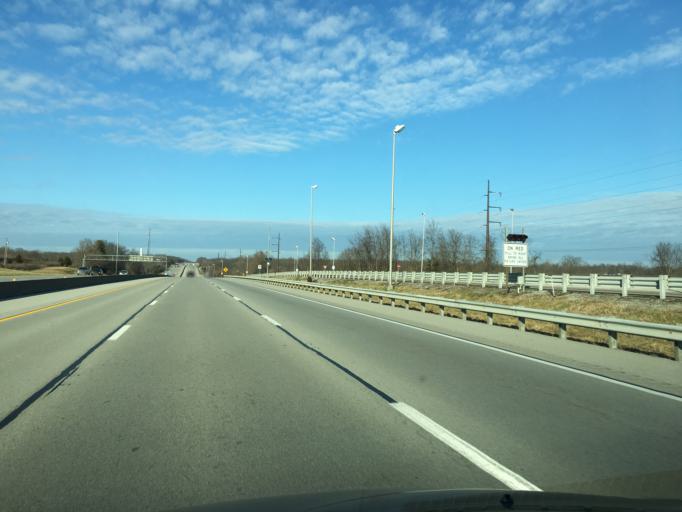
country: US
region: Kentucky
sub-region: Scott County
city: Georgetown
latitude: 38.2933
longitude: -84.5585
